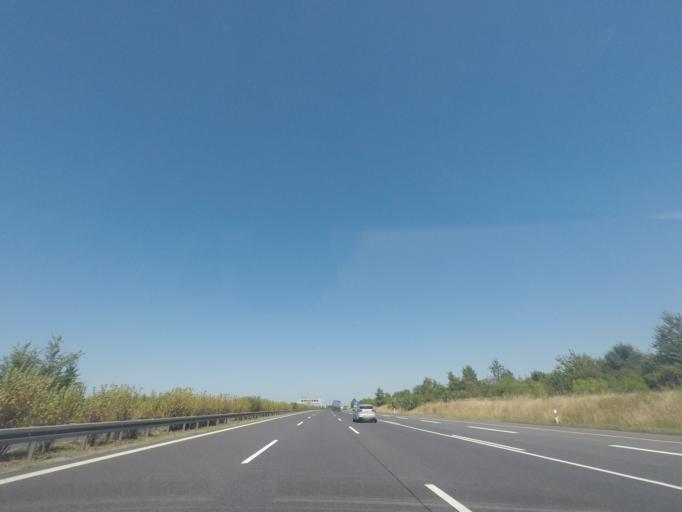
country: DE
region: Brandenburg
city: Schulzendorf
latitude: 52.3314
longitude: 13.5539
